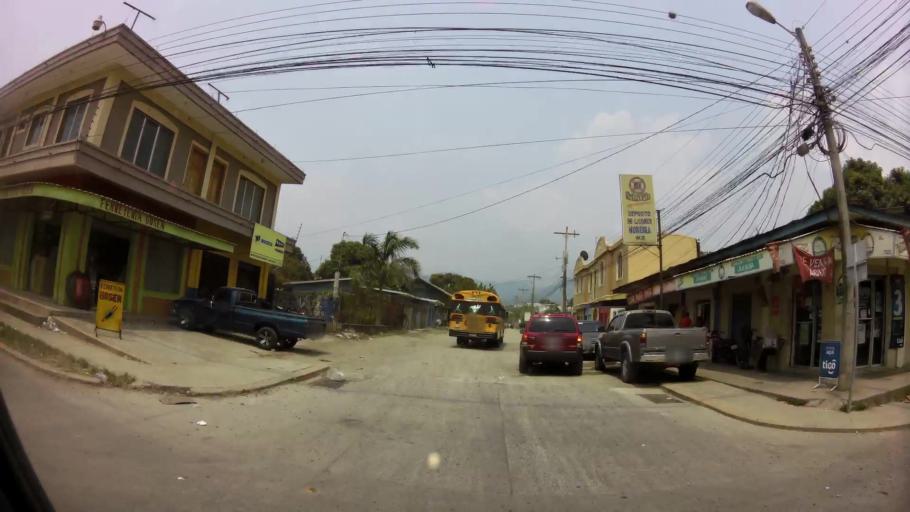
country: HN
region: Yoro
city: El Progreso
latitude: 15.4033
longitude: -87.8049
